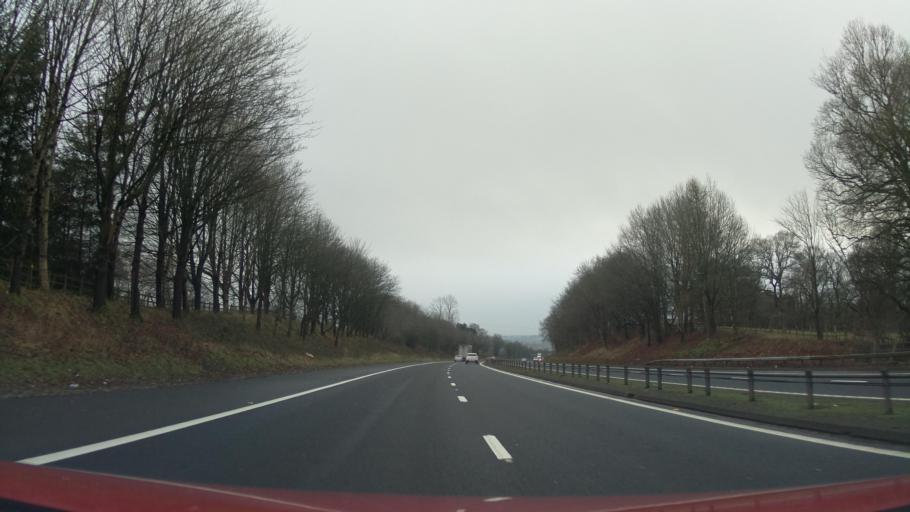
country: GB
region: Scotland
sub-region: Falkirk
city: Dunipace
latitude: 56.0440
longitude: -3.9176
